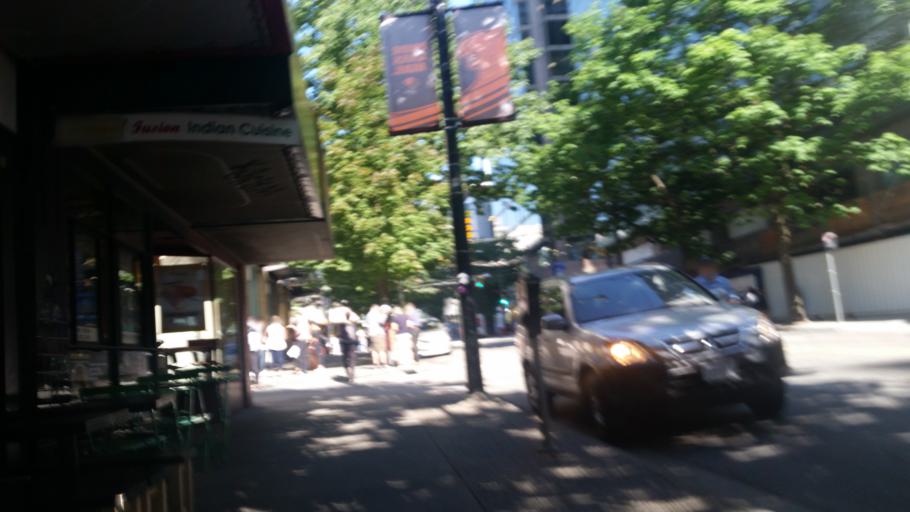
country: CA
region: British Columbia
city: West End
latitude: 49.2805
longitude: -123.1182
